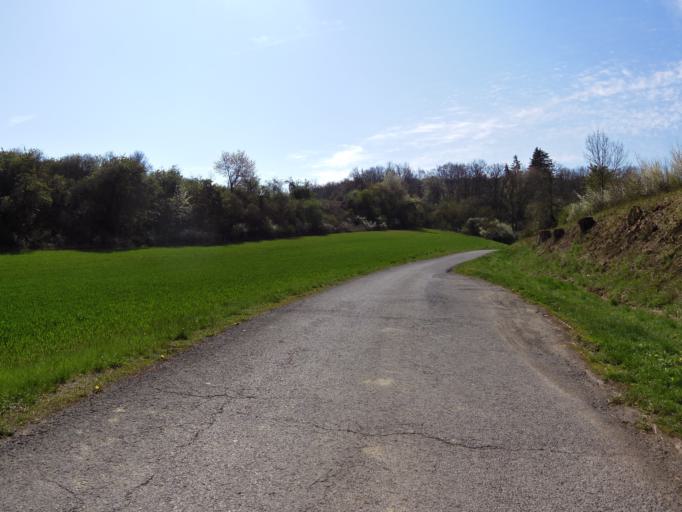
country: DE
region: Bavaria
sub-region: Regierungsbezirk Unterfranken
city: Rottendorf
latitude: 49.7812
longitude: 10.0416
